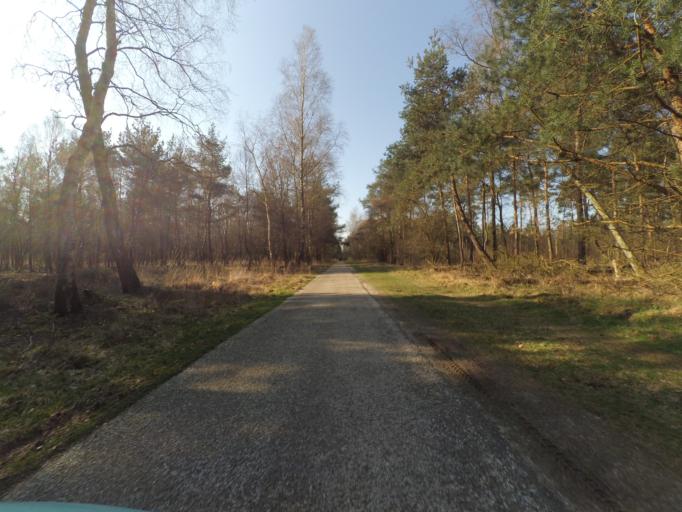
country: NL
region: Gelderland
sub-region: Gemeente Arnhem
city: Hoogkamp
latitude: 52.0516
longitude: 5.8544
